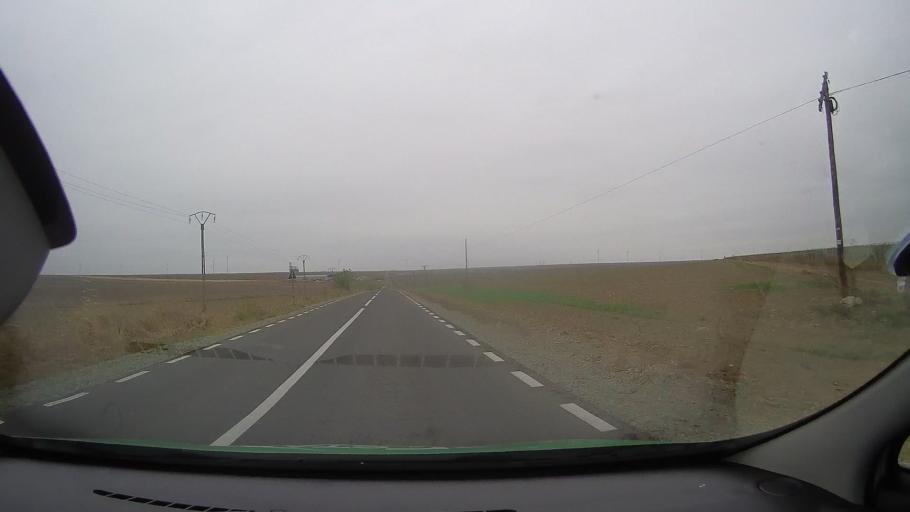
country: RO
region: Constanta
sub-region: Comuna Tortoman
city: Tortoman
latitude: 44.3575
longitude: 28.2113
